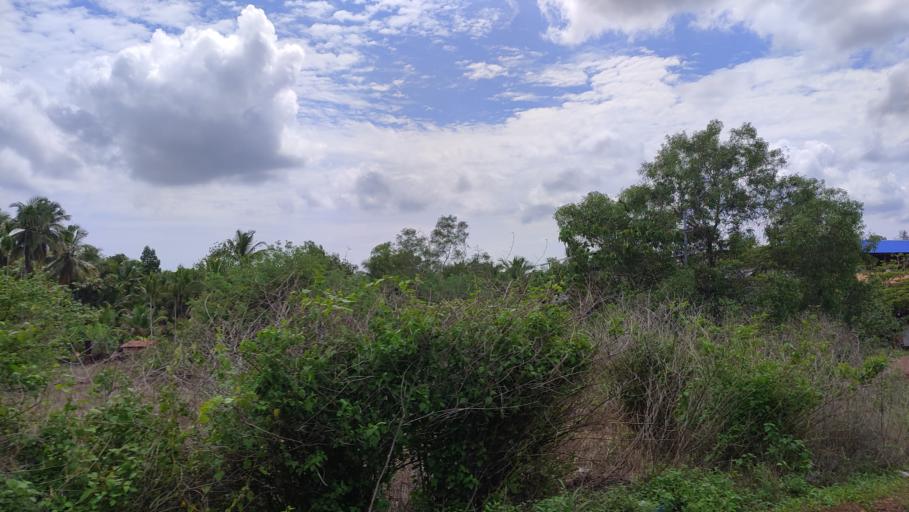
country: IN
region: Kerala
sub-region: Kasaragod District
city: Kannangad
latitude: 12.3908
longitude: 75.1014
